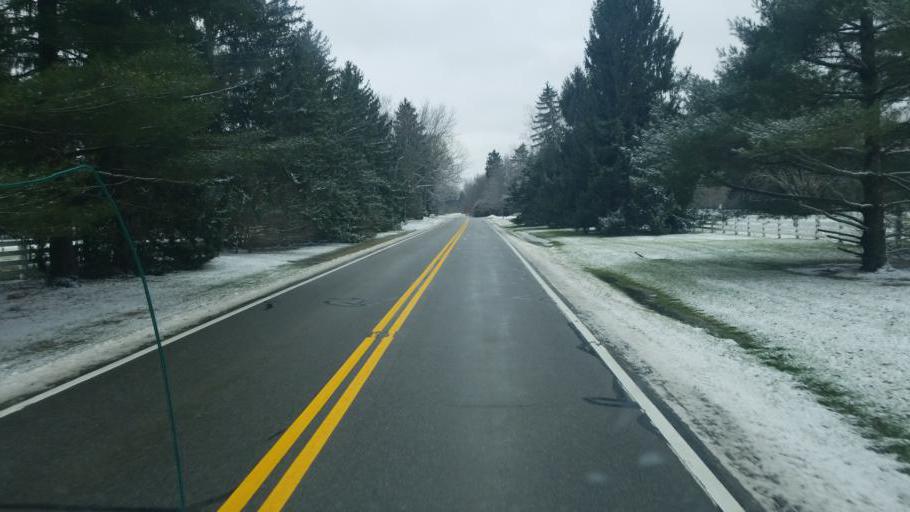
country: US
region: Ohio
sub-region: Franklin County
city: New Albany
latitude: 40.0564
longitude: -82.8011
